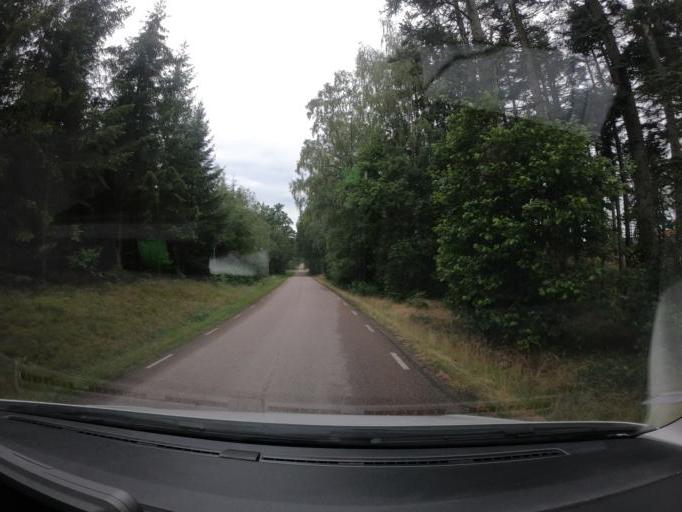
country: SE
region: Skane
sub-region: Angelholms Kommun
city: Munka-Ljungby
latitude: 56.3067
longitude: 13.0987
